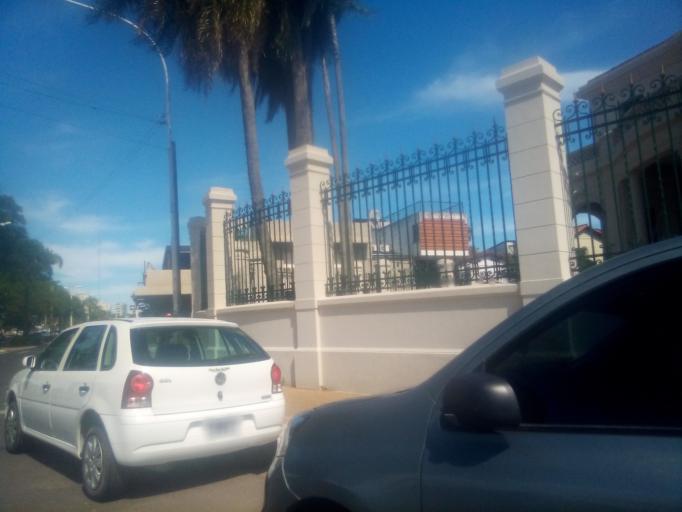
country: AR
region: Corrientes
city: Corrientes
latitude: -27.4616
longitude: -58.8416
